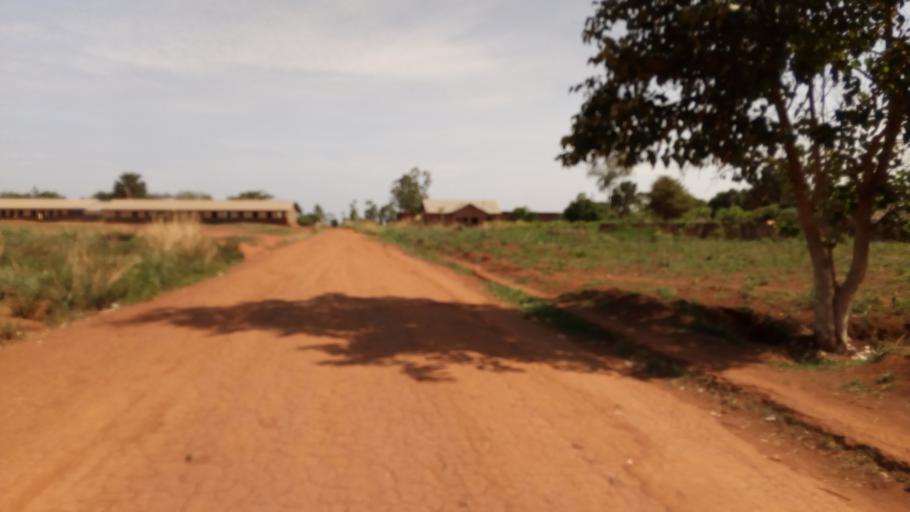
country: UG
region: Northern Region
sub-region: Gulu District
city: Gulu
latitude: 2.7889
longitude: 32.3209
